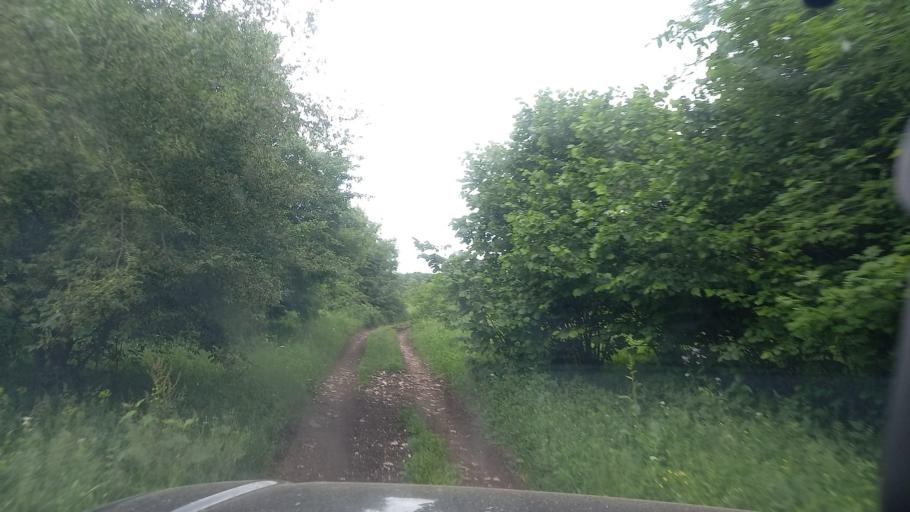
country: RU
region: Karachayevo-Cherkesiya
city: Pregradnaya
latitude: 44.0142
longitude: 41.2811
